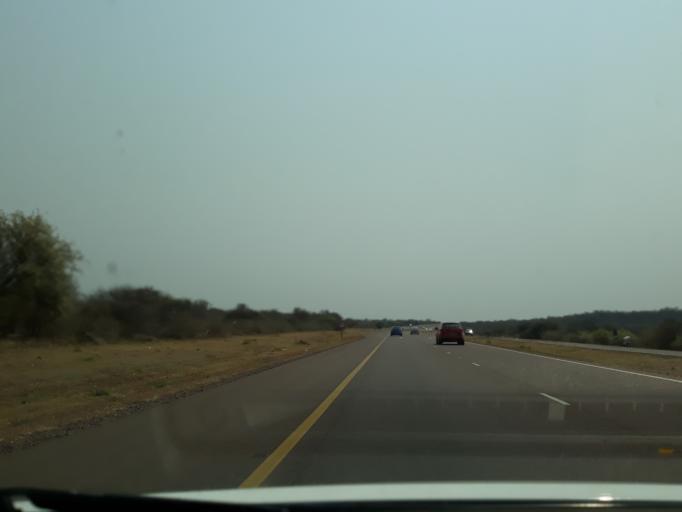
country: BW
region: Kgatleng
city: Bokaa
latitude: -24.4275
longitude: 26.0471
